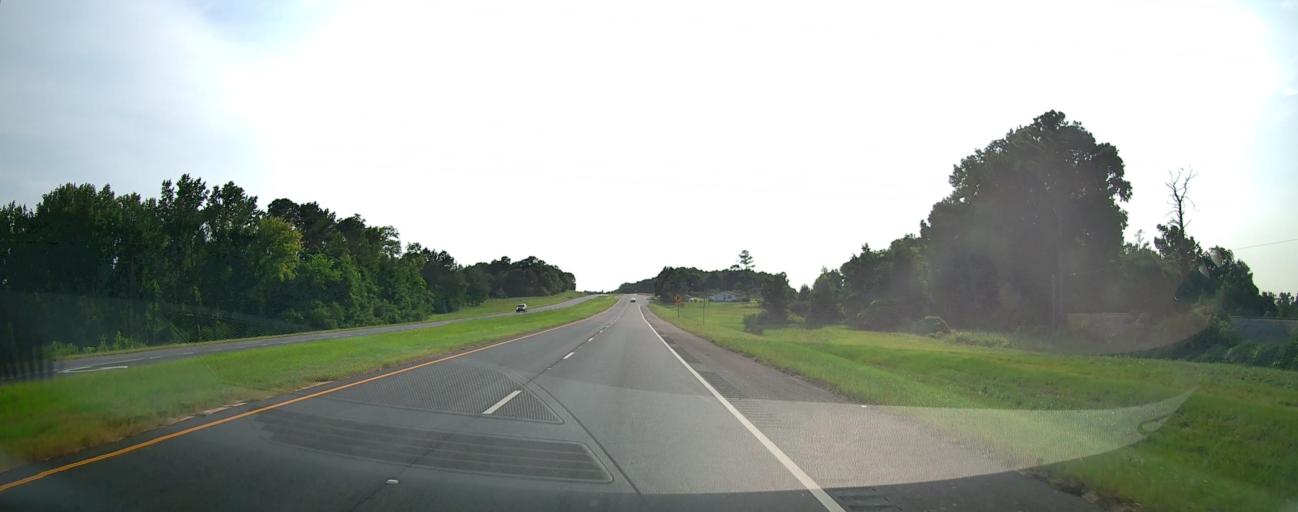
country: US
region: Georgia
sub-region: Taylor County
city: Butler
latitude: 32.5548
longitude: -84.2007
